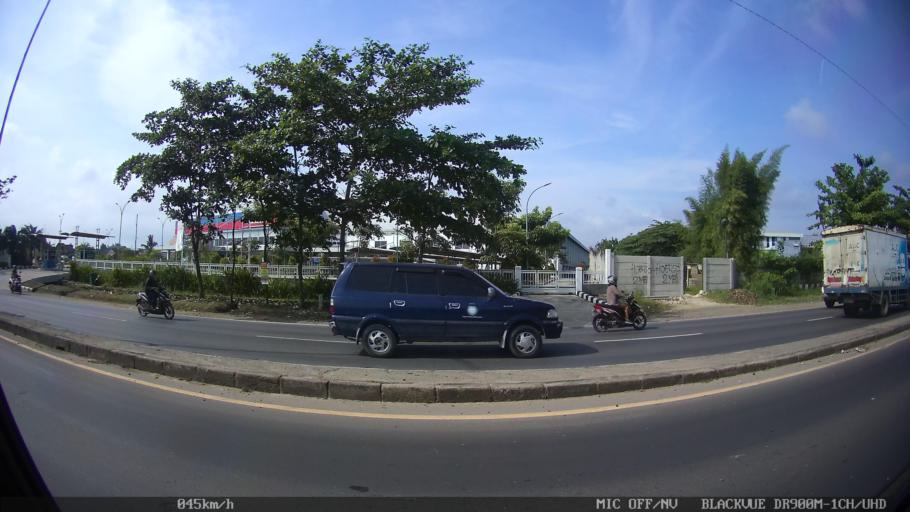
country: ID
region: Lampung
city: Kedaton
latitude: -5.3578
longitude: 105.2492
